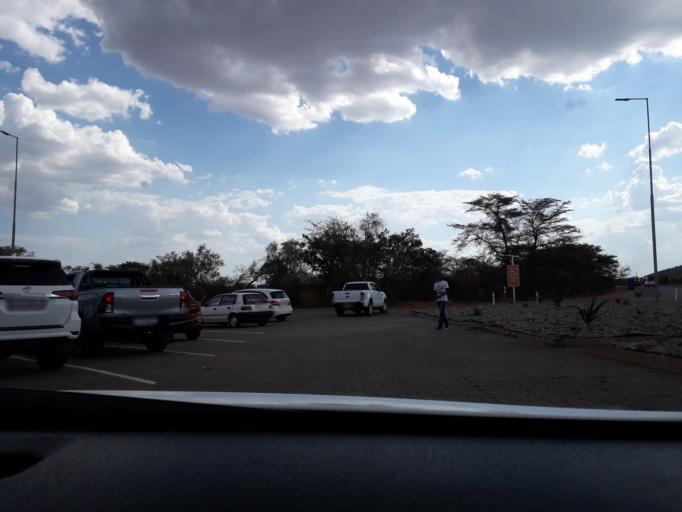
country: ZA
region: Limpopo
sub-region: Waterberg District Municipality
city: Modimolle
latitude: -24.8060
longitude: 28.4439
